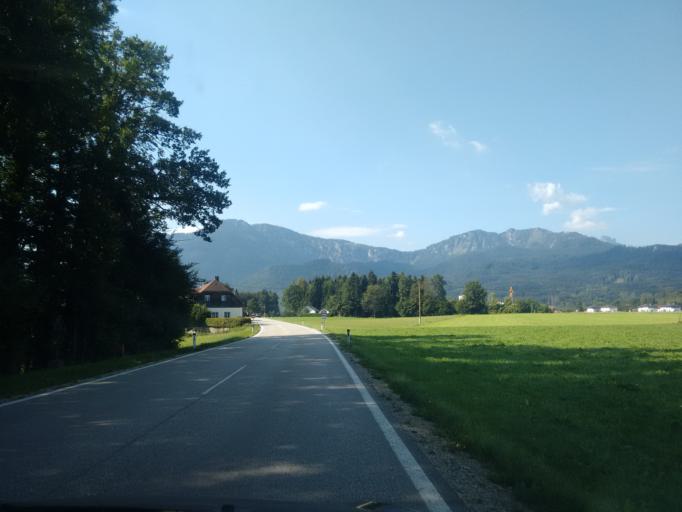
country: AT
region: Upper Austria
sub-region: Politischer Bezirk Gmunden
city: Scharnstein
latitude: 47.8946
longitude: 13.9498
